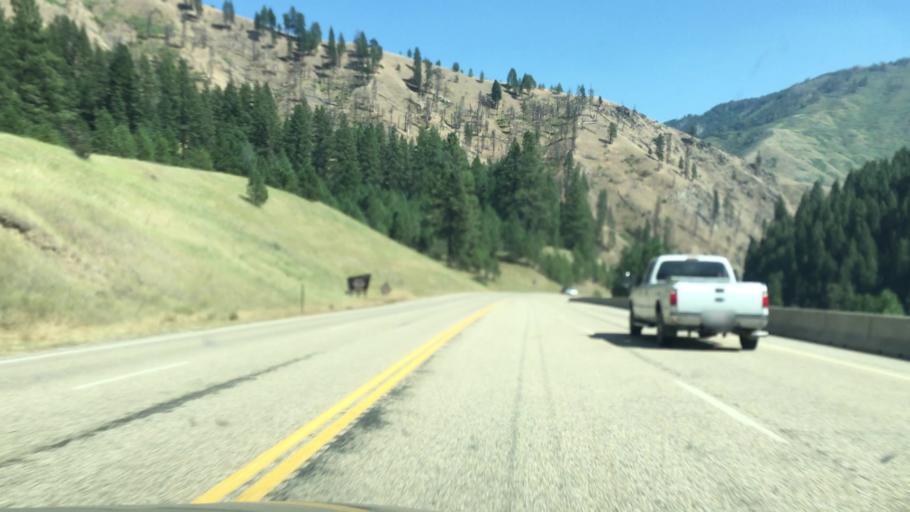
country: US
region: Idaho
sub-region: Boise County
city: Idaho City
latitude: 44.1115
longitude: -116.1016
